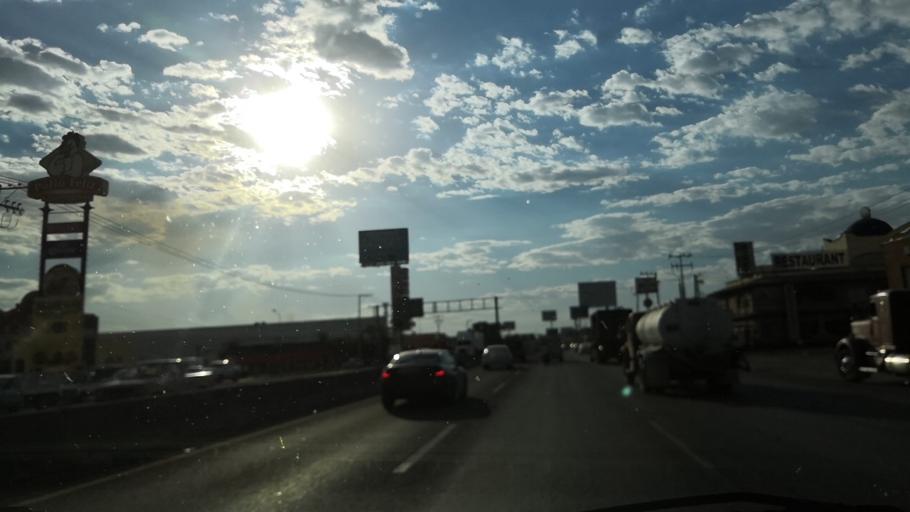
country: MX
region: Guanajuato
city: Silao
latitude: 20.9556
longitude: -101.4307
